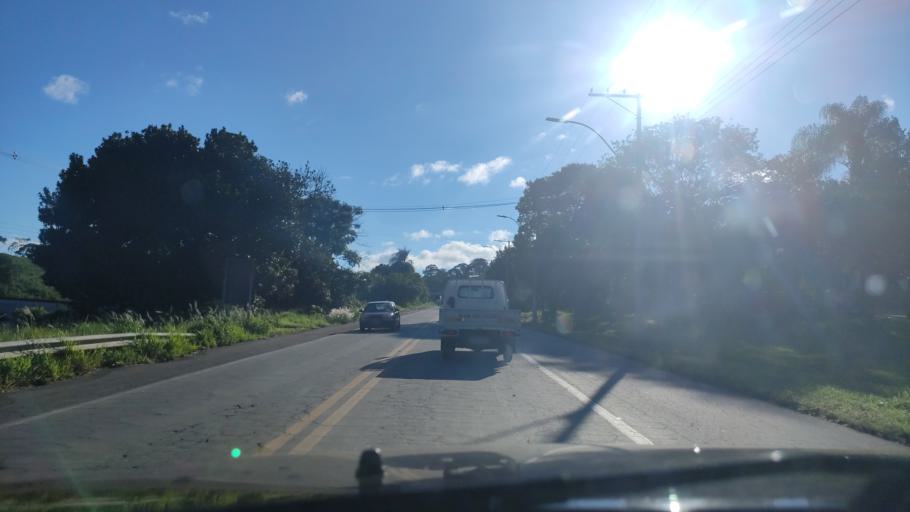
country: BR
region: Sao Paulo
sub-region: Socorro
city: Socorro
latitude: -22.5801
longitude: -46.5206
